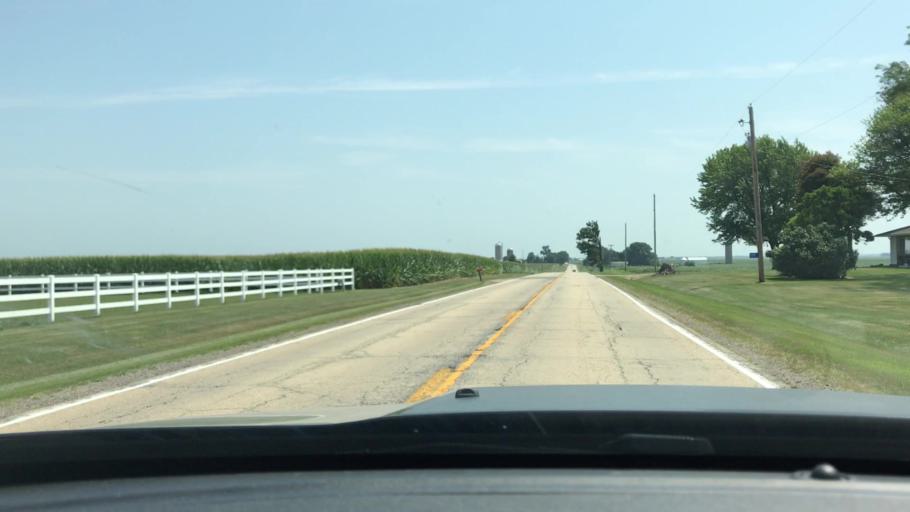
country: US
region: Illinois
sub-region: LaSalle County
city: Earlville
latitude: 41.4690
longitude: -88.9270
